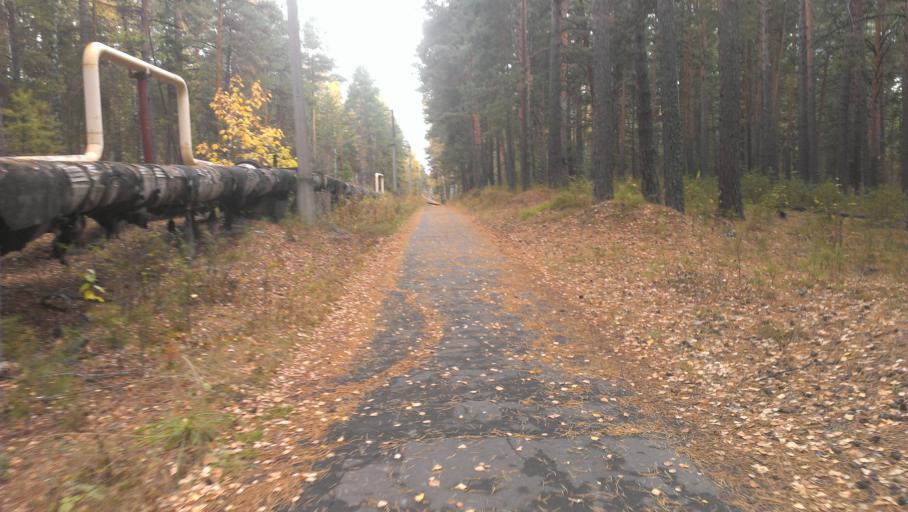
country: RU
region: Altai Krai
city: Yuzhnyy
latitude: 53.2665
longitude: 83.6838
